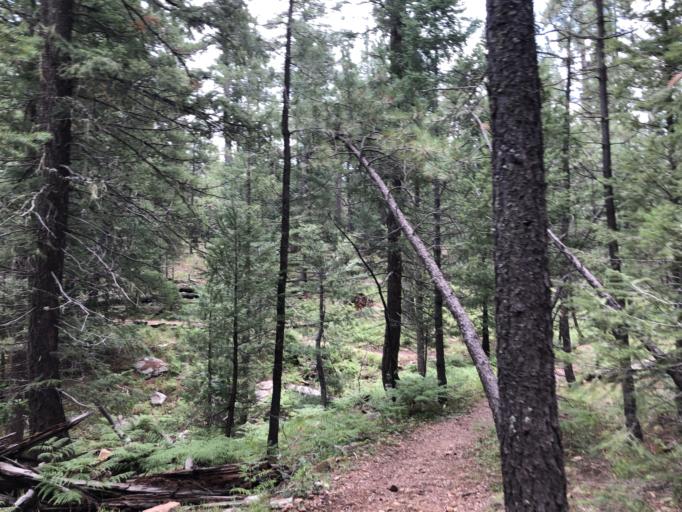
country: US
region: Arizona
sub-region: Gila County
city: Star Valley
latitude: 34.3380
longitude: -110.9525
